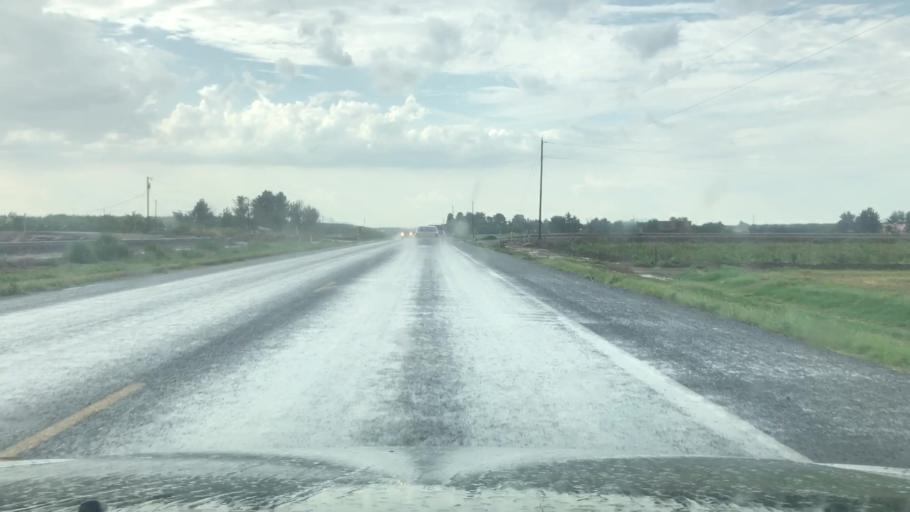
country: US
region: New Mexico
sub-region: Dona Ana County
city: Mesquite
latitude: 32.1752
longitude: -106.7033
